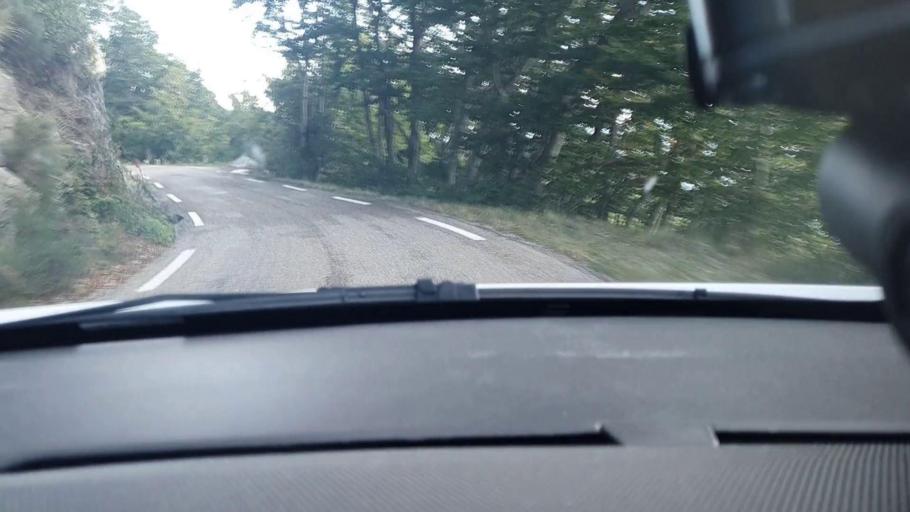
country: FR
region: Languedoc-Roussillon
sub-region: Departement du Gard
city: Branoux-les-Taillades
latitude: 44.3664
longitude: 3.9188
